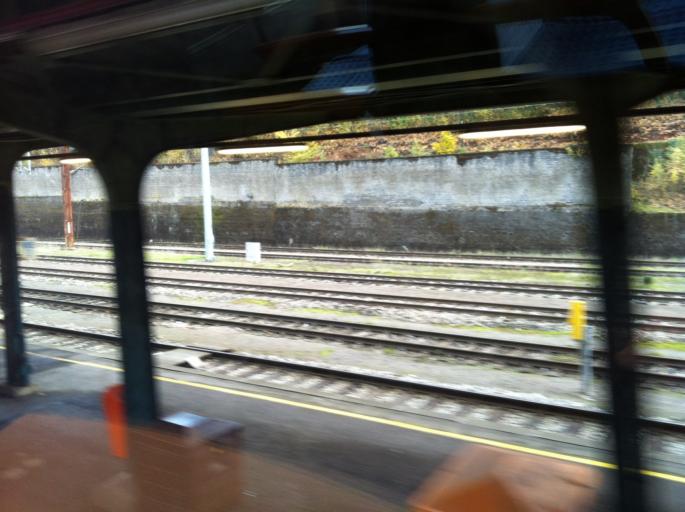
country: LU
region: Luxembourg
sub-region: Canton d'Esch-sur-Alzette
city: Esch-sur-Alzette
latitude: 49.4937
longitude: 5.9853
